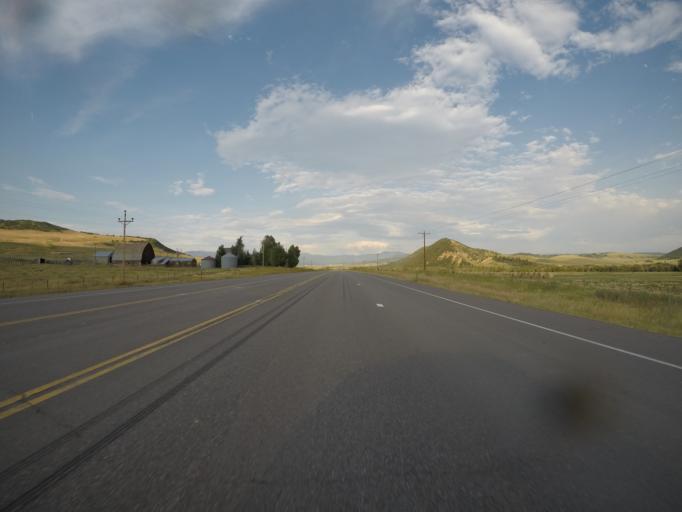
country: US
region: Colorado
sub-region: Routt County
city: Steamboat Springs
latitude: 40.4857
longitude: -107.0080
